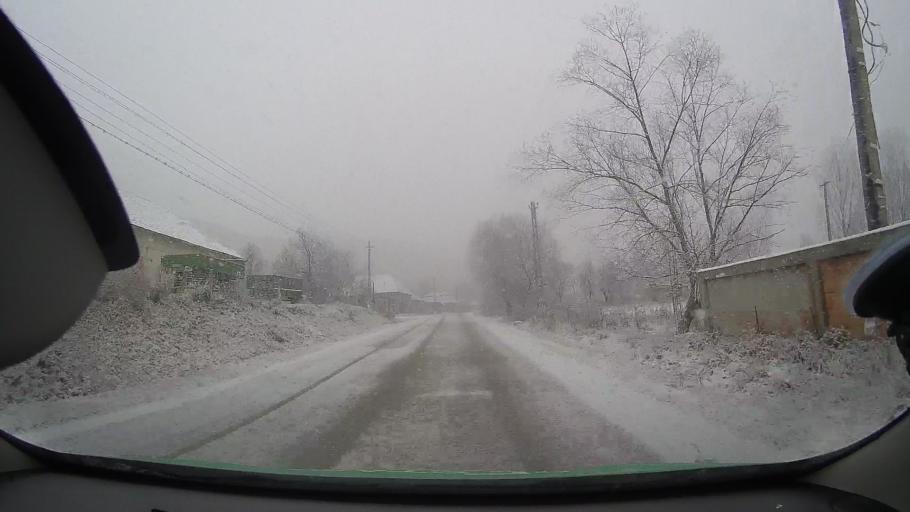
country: RO
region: Alba
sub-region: Comuna Hoparta
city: Hoparta
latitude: 46.3162
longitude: 23.8621
